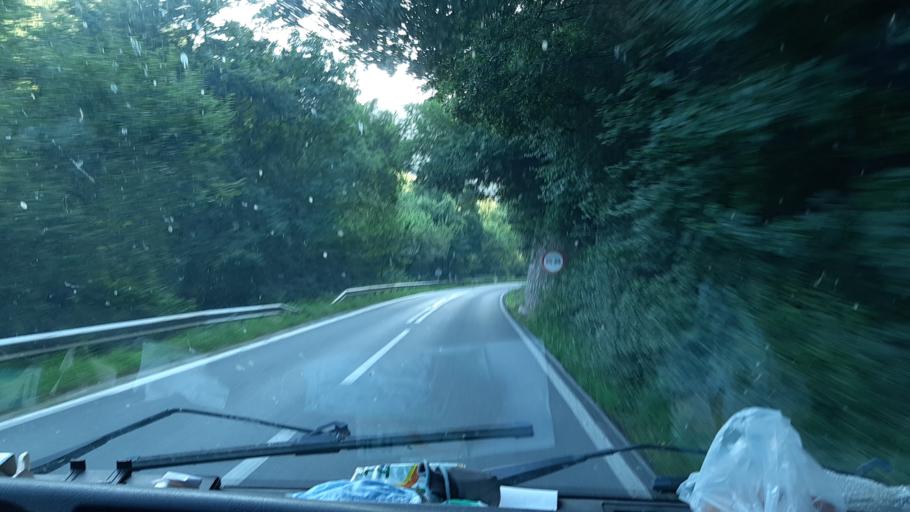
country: RO
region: Caras-Severin
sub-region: Municipiul Resita
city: Calnic
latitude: 45.3553
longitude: 21.8258
